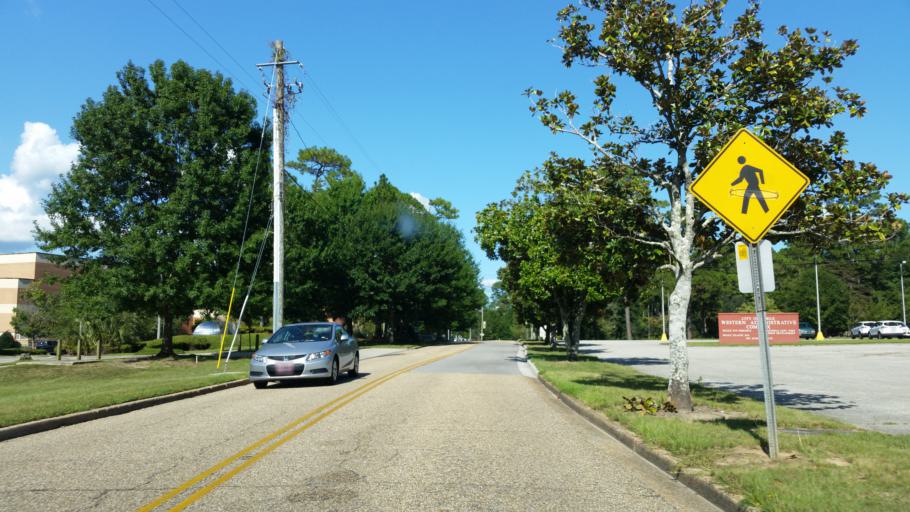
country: US
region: Alabama
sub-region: Mobile County
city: Prichard
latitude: 30.7034
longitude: -88.1557
